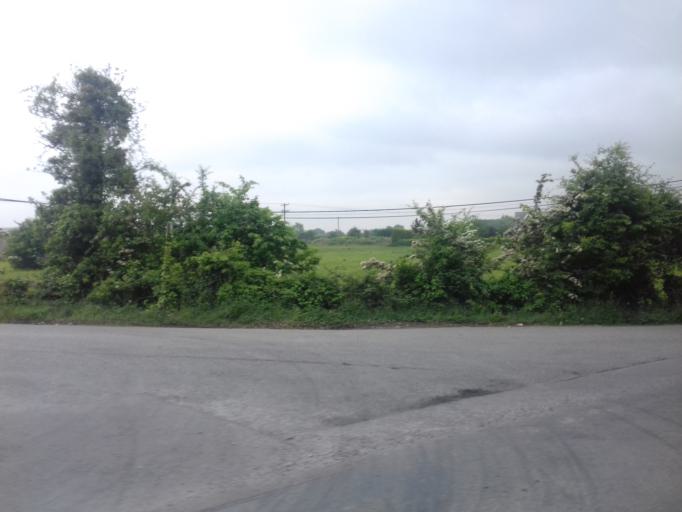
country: IE
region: Leinster
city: Donabate
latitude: 53.4808
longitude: -6.1610
